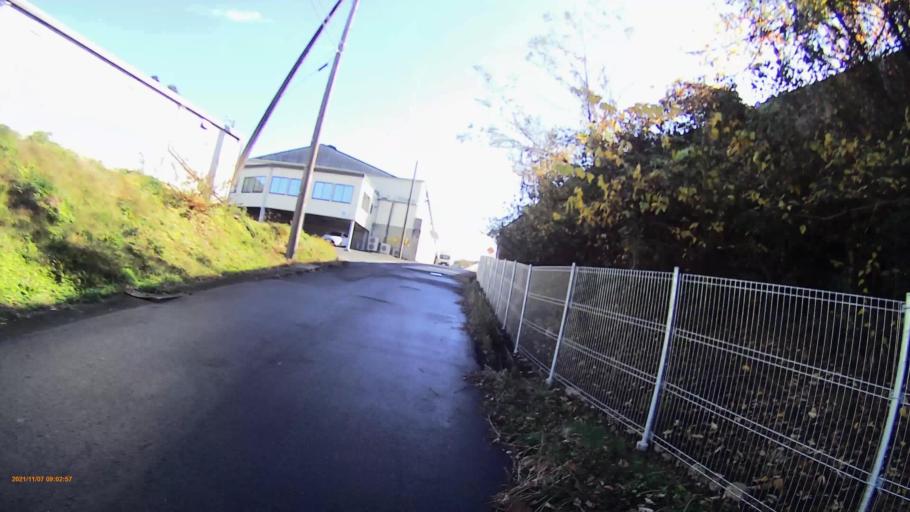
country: JP
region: Gifu
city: Mizunami
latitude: 35.4368
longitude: 137.3479
